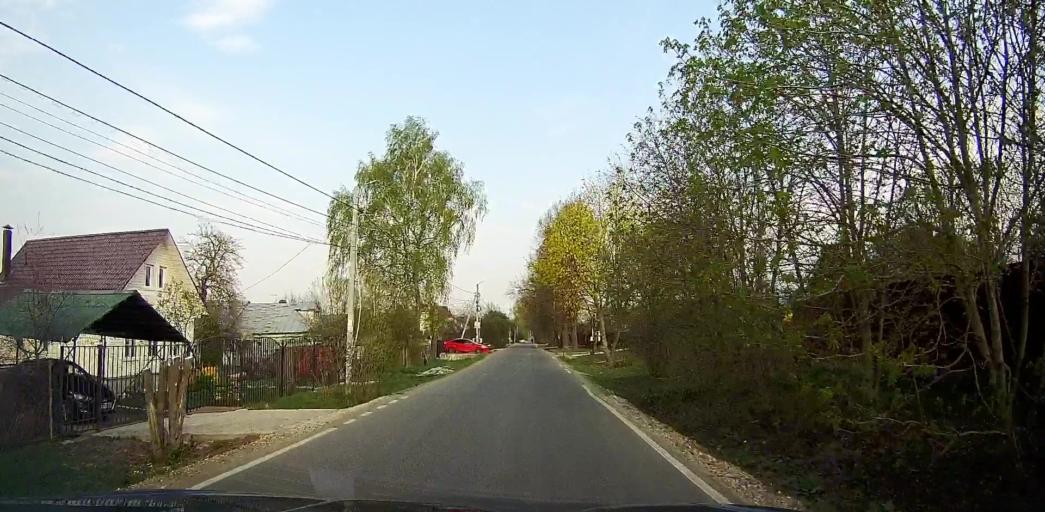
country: RU
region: Moskovskaya
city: Andreyevskoye
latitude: 55.5549
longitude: 37.9273
